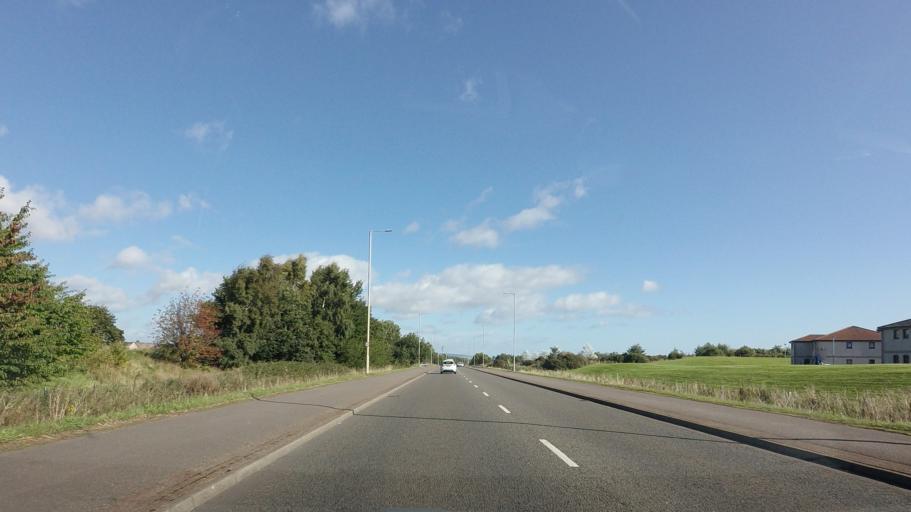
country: GB
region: Scotland
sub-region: Highland
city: Inverness
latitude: 57.4629
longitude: -4.1968
